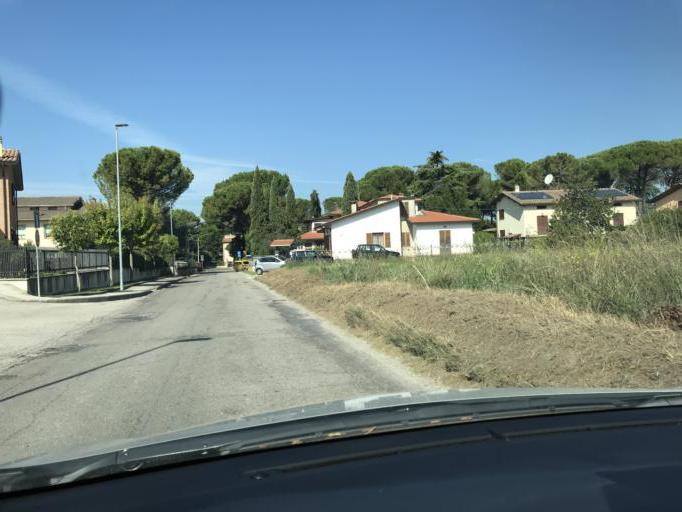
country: IT
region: Umbria
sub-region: Provincia di Perugia
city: Ponte Felcino
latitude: 43.1079
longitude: 12.4610
